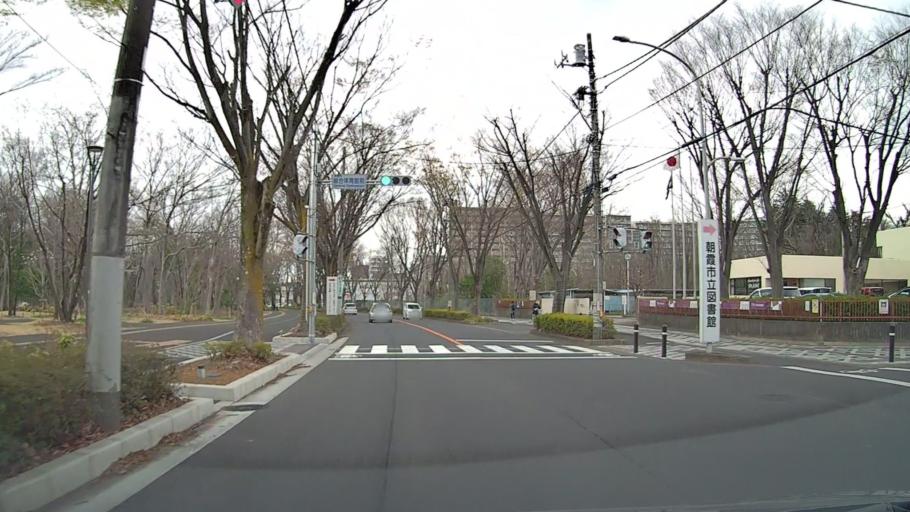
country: JP
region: Saitama
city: Asaka
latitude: 35.7934
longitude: 139.5945
